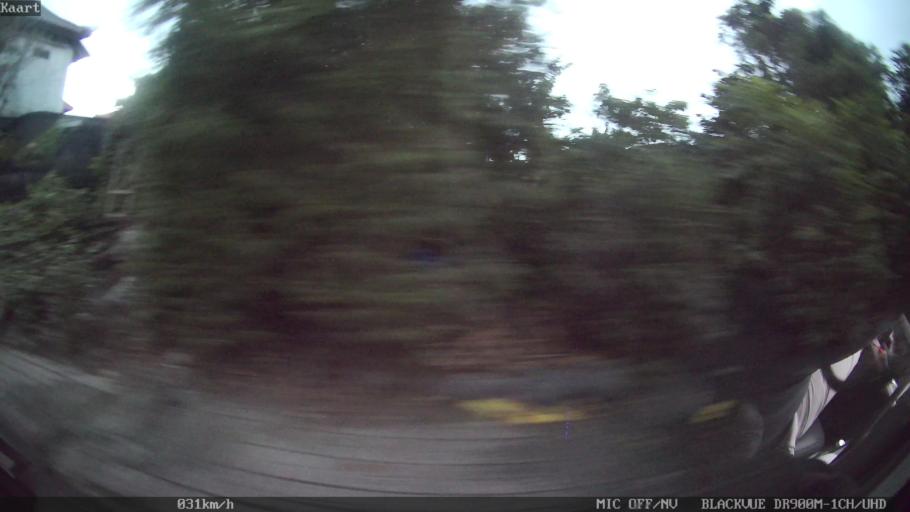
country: ID
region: Bali
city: Banjar Pasekan
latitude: -8.6046
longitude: 115.2820
